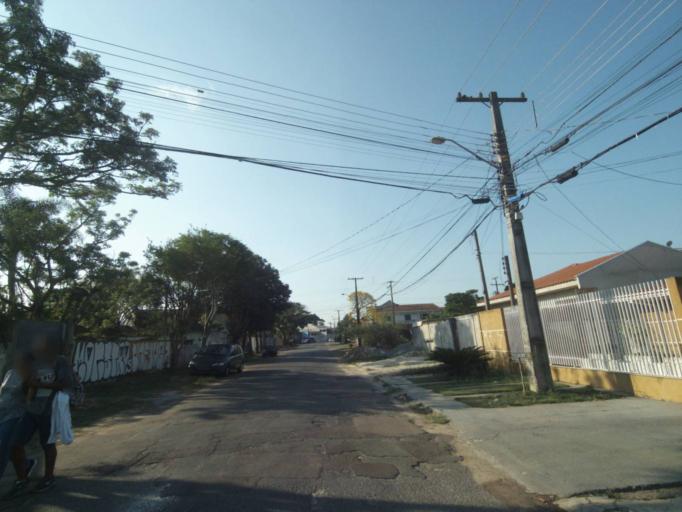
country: BR
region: Parana
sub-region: Curitiba
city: Curitiba
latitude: -25.4835
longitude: -49.3345
